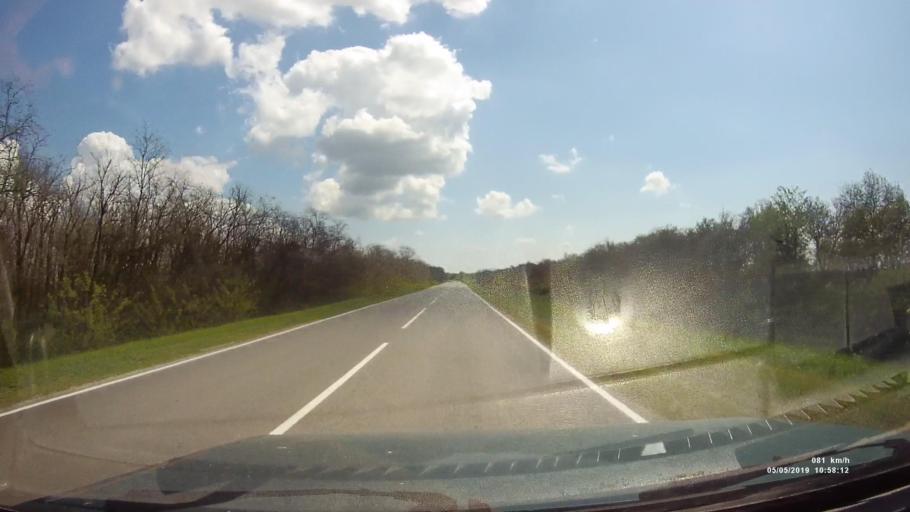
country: RU
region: Rostov
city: Ust'-Donetskiy
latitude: 47.6703
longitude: 40.8488
